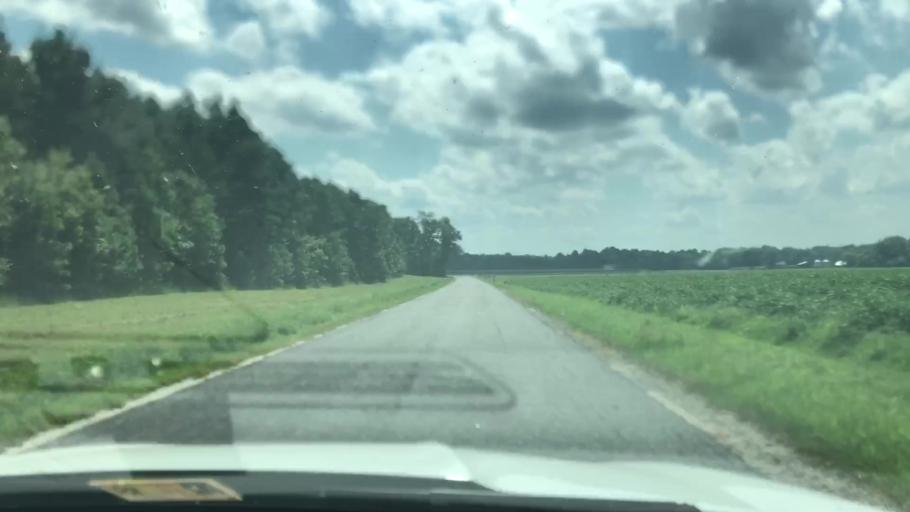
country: US
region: Virginia
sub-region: Middlesex County
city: Saluda
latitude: 37.6738
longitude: -76.6819
